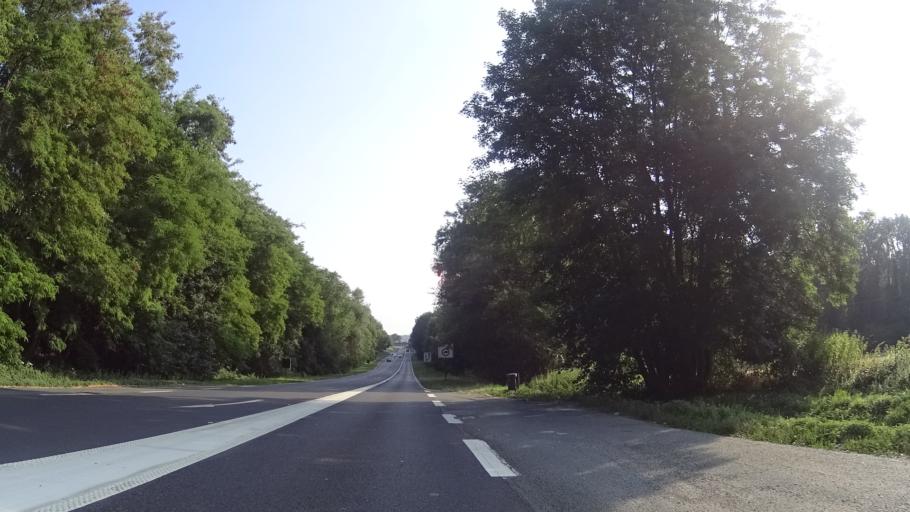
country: FR
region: Ile-de-France
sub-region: Departement du Val-d'Oise
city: Luzarches
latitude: 49.1056
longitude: 2.4256
